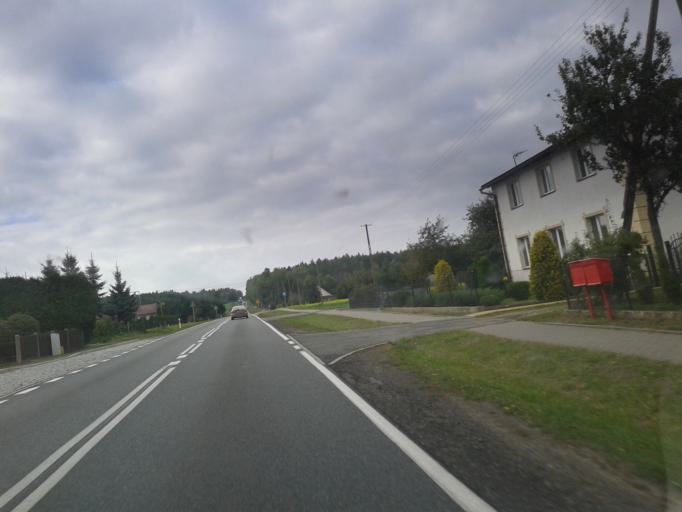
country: PL
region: Kujawsko-Pomorskie
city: Kamien Krajenski
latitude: 53.5411
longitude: 17.5176
